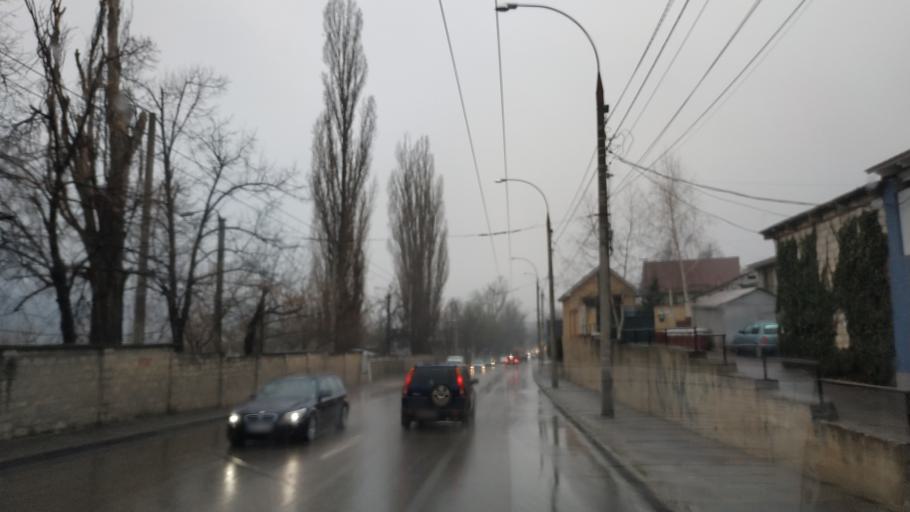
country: MD
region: Chisinau
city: Vatra
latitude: 47.0239
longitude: 28.7871
